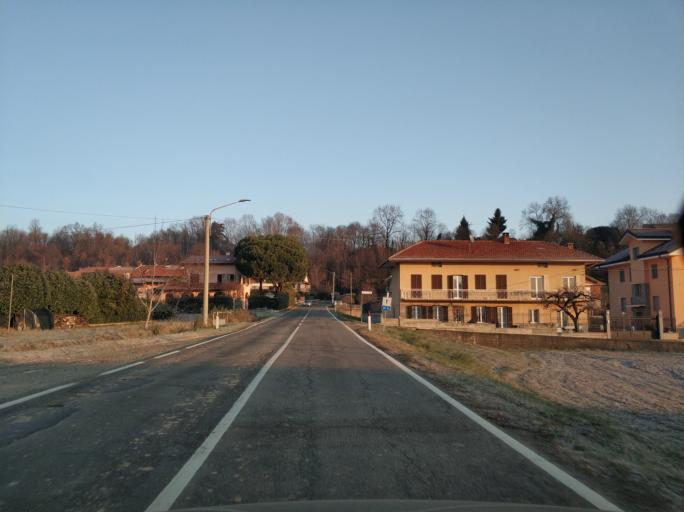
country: IT
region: Piedmont
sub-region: Provincia di Torino
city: Nole
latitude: 45.2547
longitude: 7.5761
